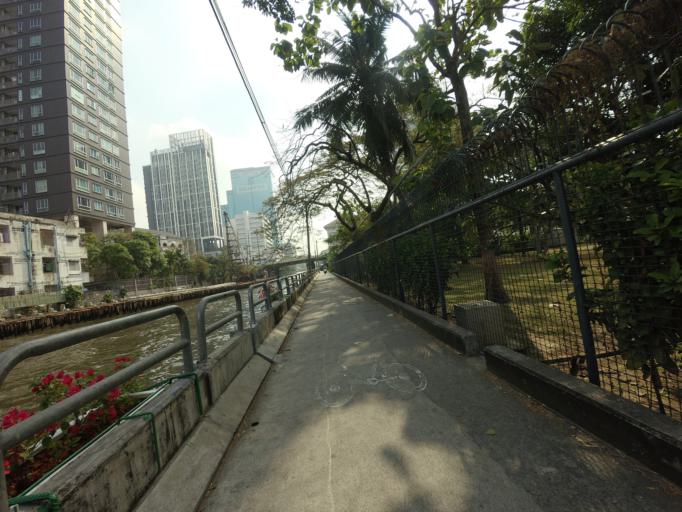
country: TH
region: Bangkok
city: Watthana
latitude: 13.7428
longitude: 100.5845
